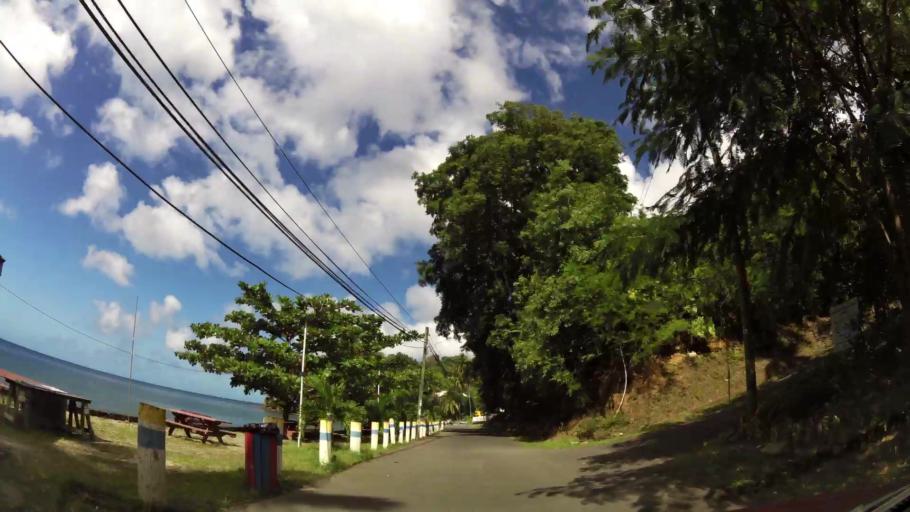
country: DM
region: Saint John
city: Portsmouth
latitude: 15.6105
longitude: -61.4643
